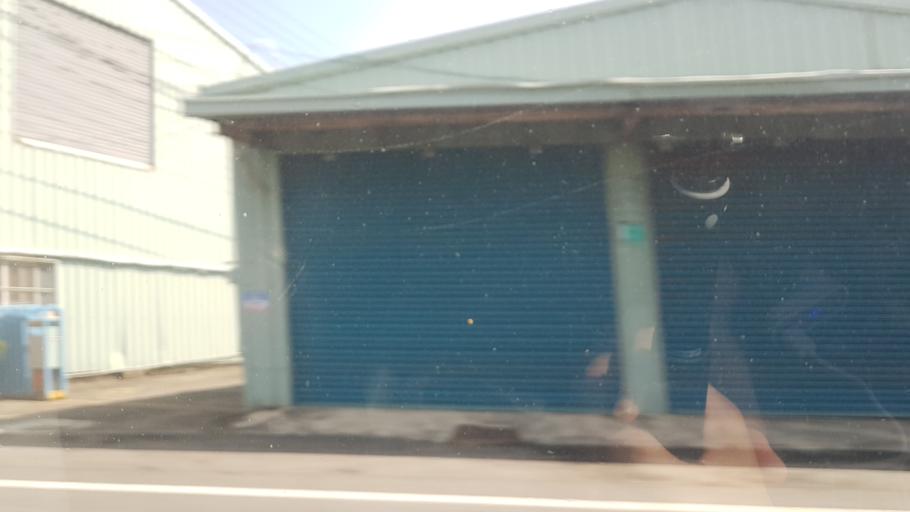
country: TW
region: Taiwan
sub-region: Tainan
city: Tainan
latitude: 22.9439
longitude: 120.2502
